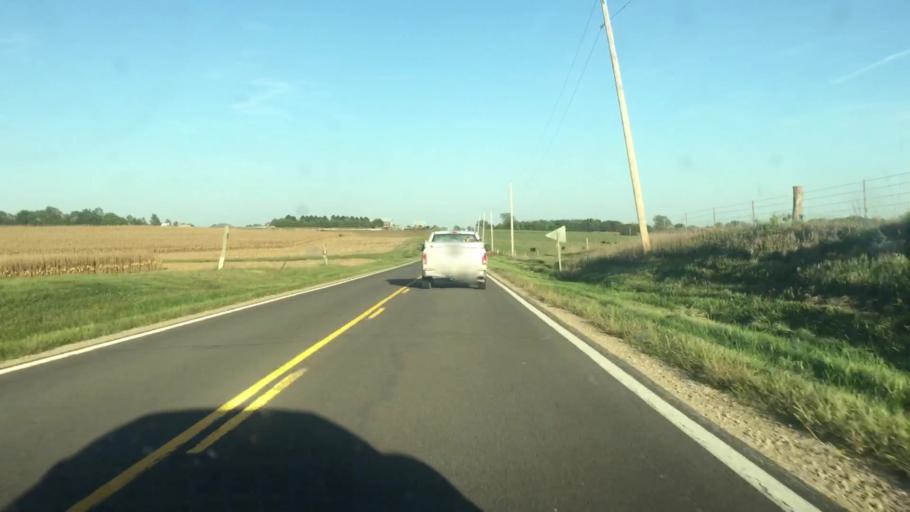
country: US
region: Kansas
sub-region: Brown County
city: Horton
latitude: 39.5512
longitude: -95.4181
